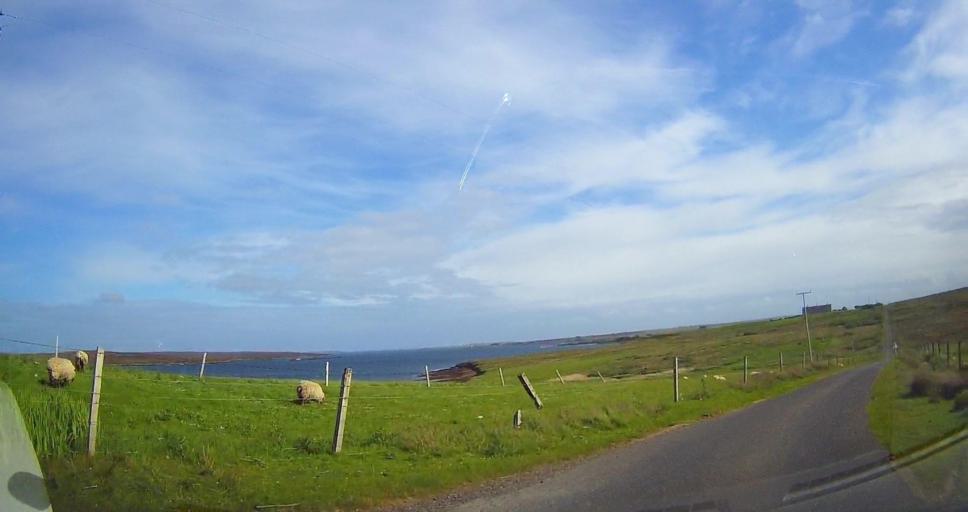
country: GB
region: Scotland
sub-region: Orkney Islands
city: Stromness
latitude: 58.8531
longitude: -3.2033
